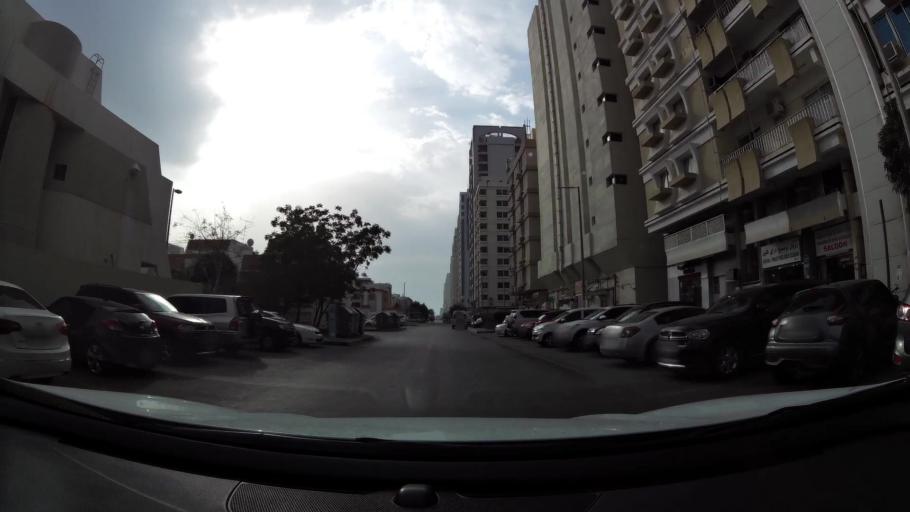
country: AE
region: Abu Dhabi
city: Abu Dhabi
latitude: 24.4668
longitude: 54.3748
